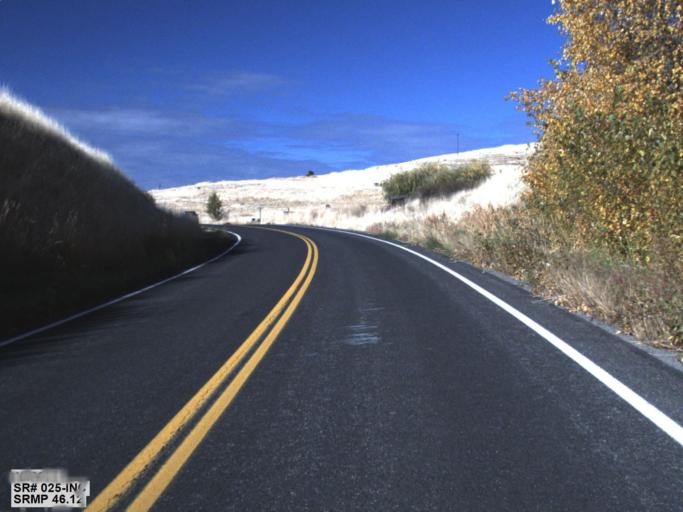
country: US
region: Washington
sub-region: Stevens County
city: Kettle Falls
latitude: 48.1579
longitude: -118.1668
